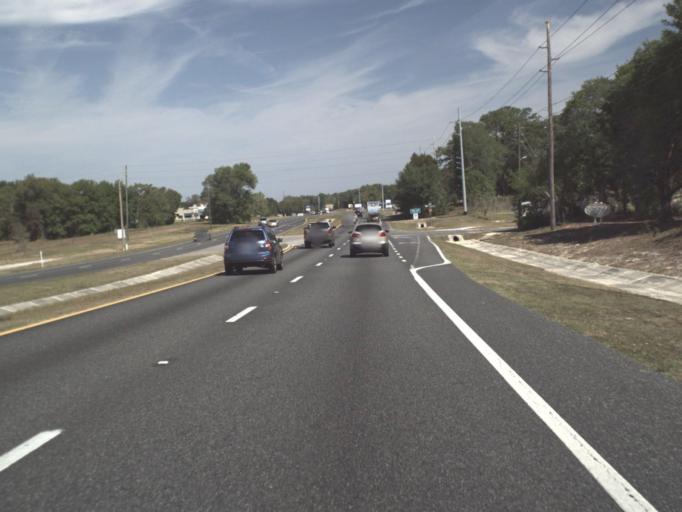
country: US
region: Florida
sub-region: Lake County
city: Lady Lake
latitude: 28.8933
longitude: -81.9080
